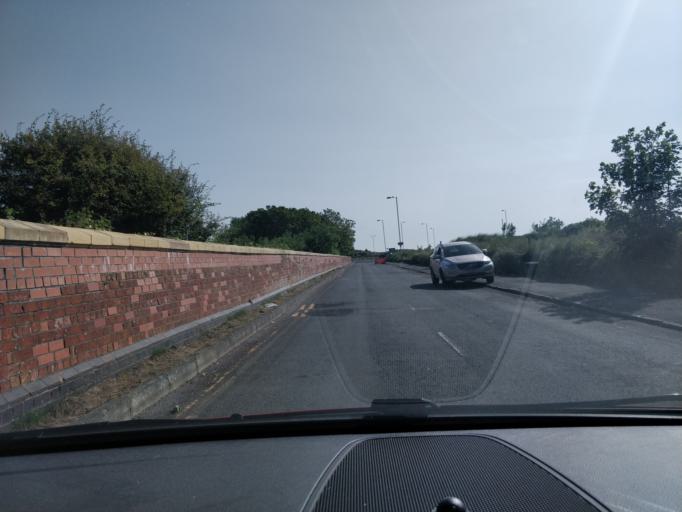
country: GB
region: England
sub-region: Sefton
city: Southport
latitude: 53.6410
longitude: -3.0261
